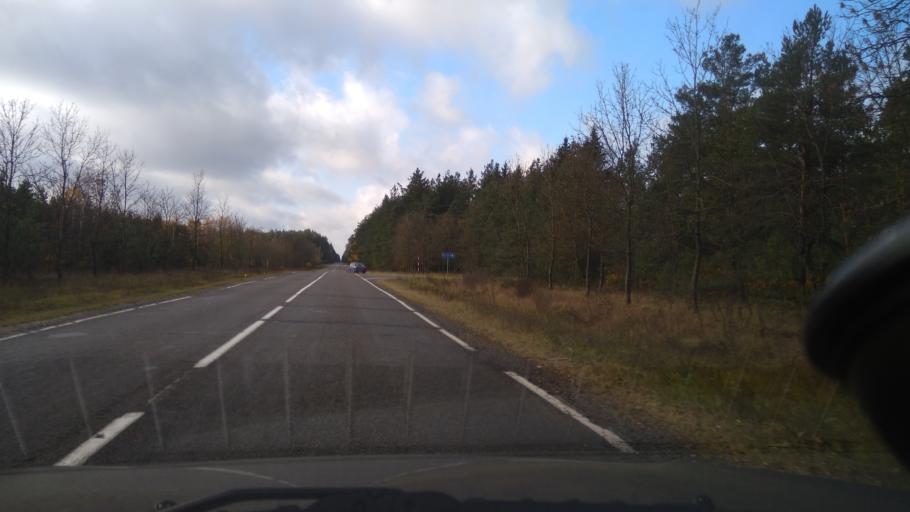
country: BY
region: Minsk
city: Slutsk
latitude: 53.2291
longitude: 27.7137
